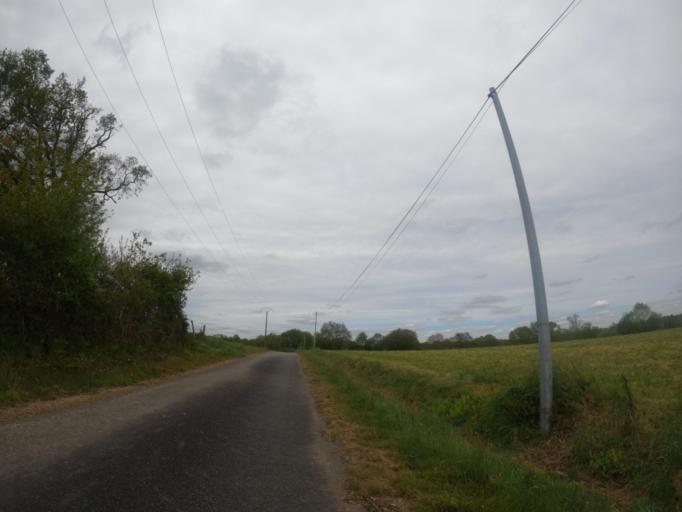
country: FR
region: Pays de la Loire
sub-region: Departement de la Loire-Atlantique
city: Saint-Aubin-des-Chateaux
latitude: 47.7276
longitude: -1.4499
